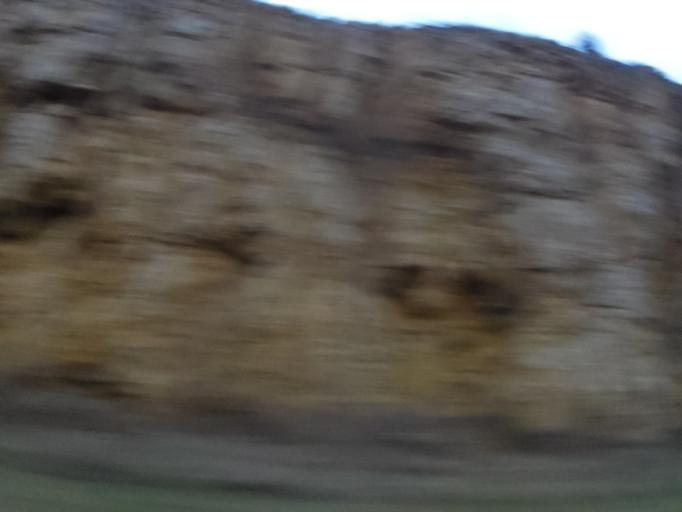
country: US
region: Wisconsin
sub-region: Saint Croix County
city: Hudson
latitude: 44.9538
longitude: -92.7145
